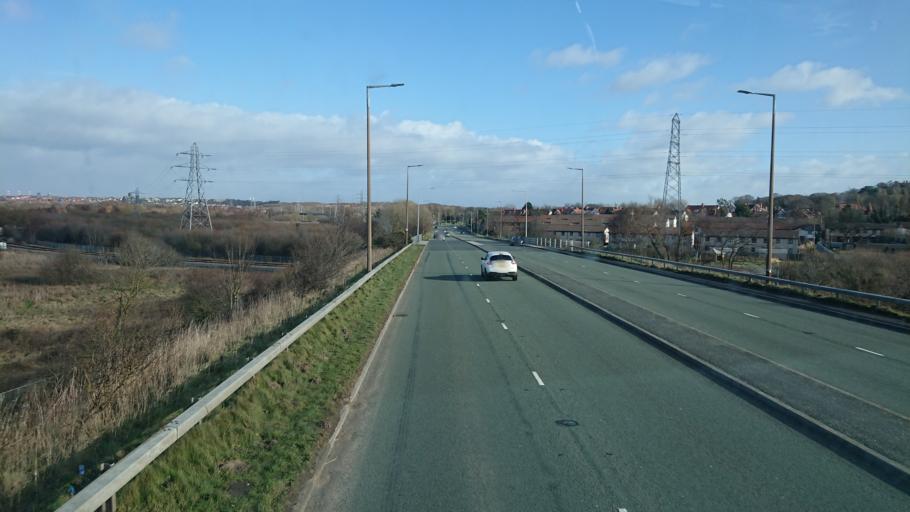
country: GB
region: England
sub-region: Metropolitan Borough of Wirral
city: Wallasey
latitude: 53.4059
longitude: -3.0852
